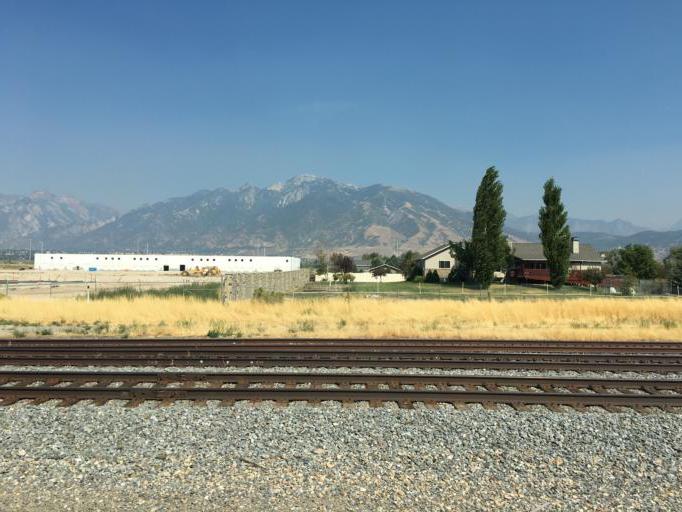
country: US
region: Utah
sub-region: Salt Lake County
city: Riverton
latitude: 40.5167
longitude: -111.9044
